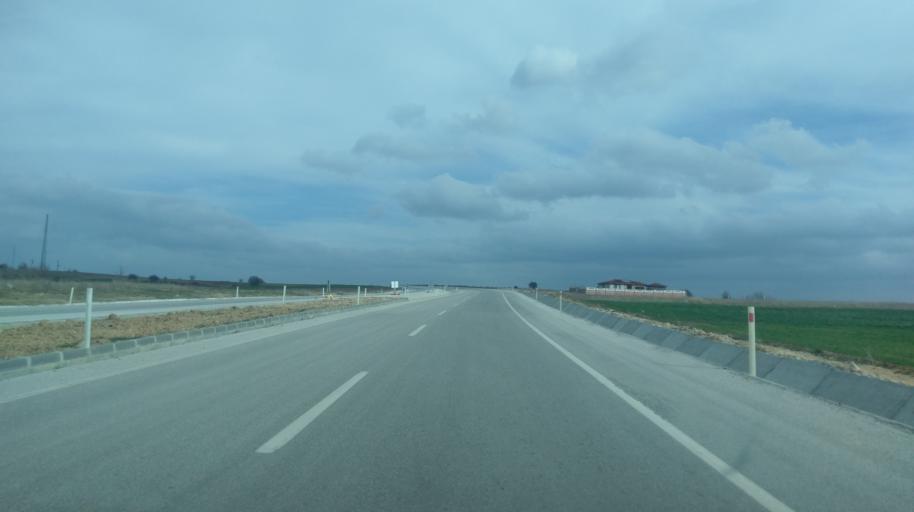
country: TR
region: Kirklareli
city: Inece
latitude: 41.6804
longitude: 27.0983
